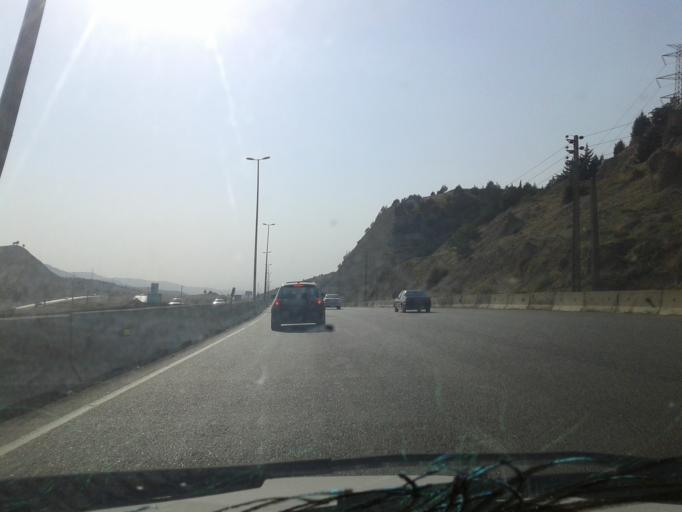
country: IR
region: Tehran
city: Tehran
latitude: 35.7332
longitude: 51.6567
